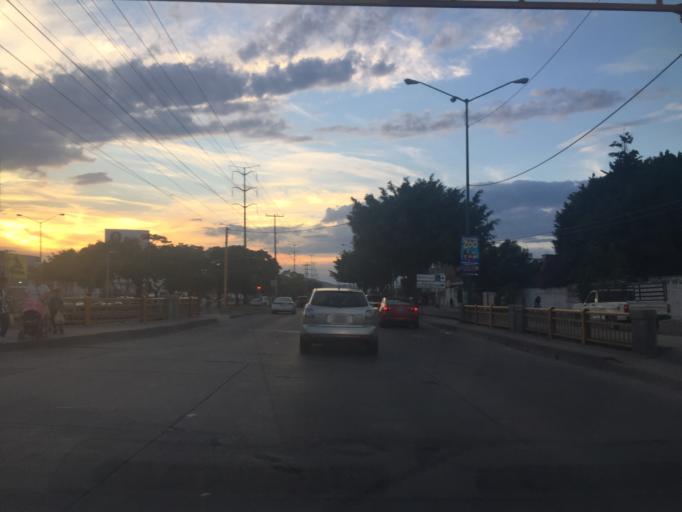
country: MX
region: Guanajuato
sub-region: Leon
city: Medina
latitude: 21.1446
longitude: -101.6445
